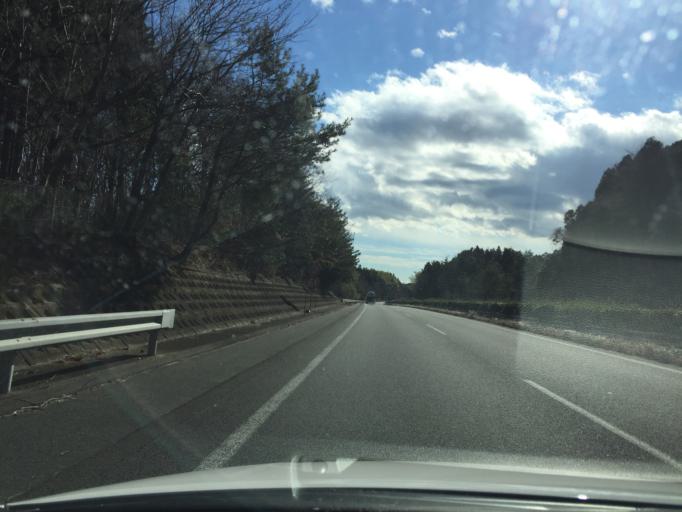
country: JP
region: Fukushima
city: Iwaki
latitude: 37.0179
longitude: 140.8135
